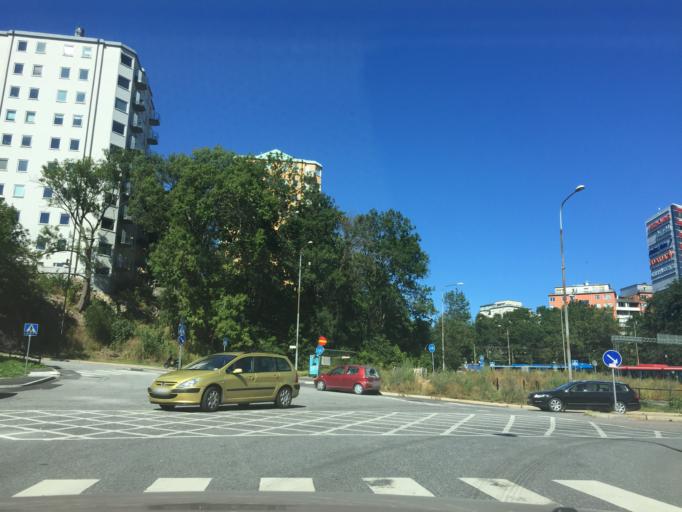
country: SE
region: Stockholm
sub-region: Stockholms Kommun
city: OEstermalm
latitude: 59.3115
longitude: 18.1067
